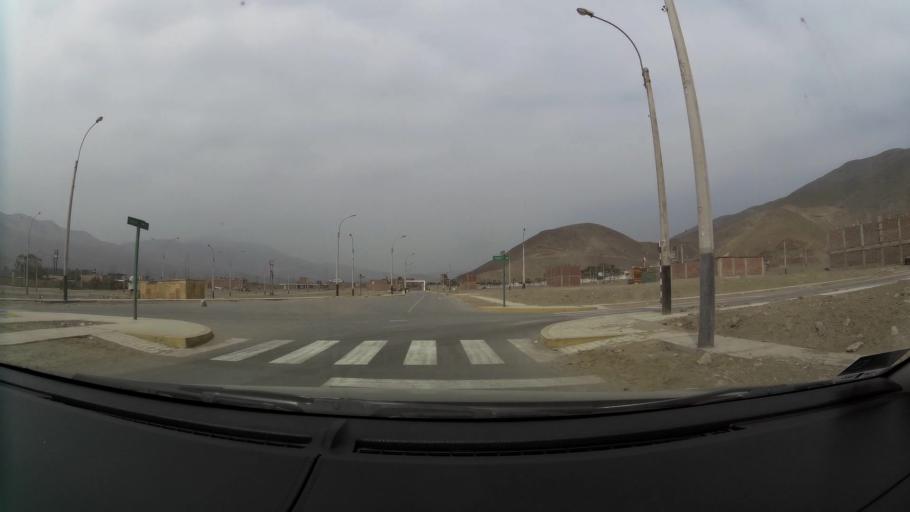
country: PE
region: Lima
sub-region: Lima
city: Santa Rosa
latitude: -11.7932
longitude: -77.1495
